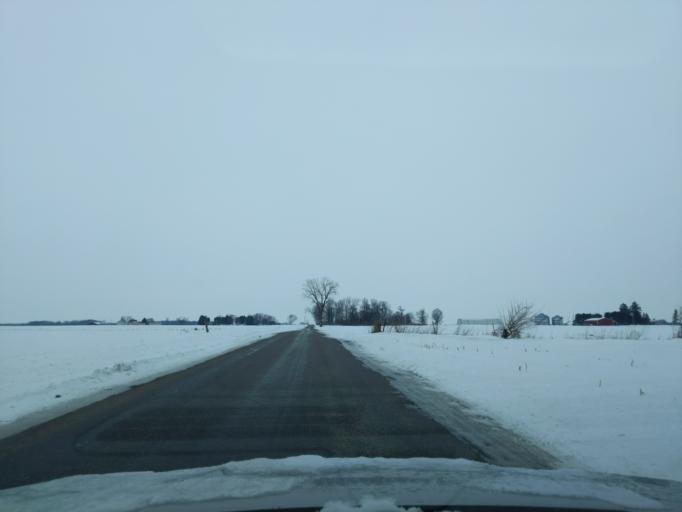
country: US
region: Indiana
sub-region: Benton County
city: Otterbein
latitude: 40.4384
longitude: -87.0927
